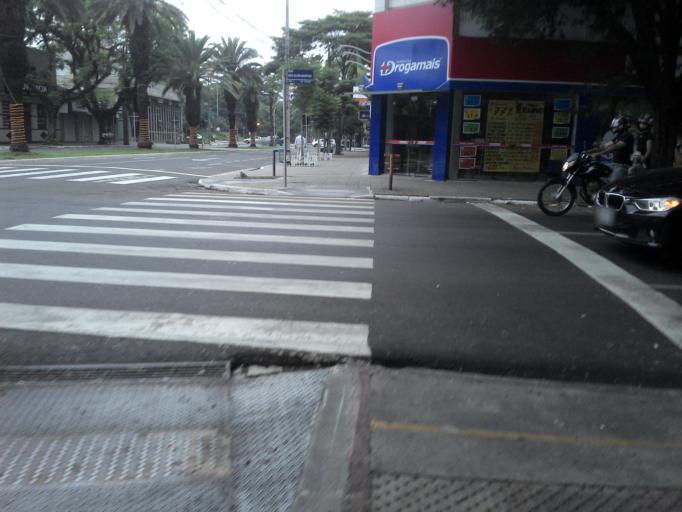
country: BR
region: Parana
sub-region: Maringa
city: Maringa
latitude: -23.4226
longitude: -51.9401
